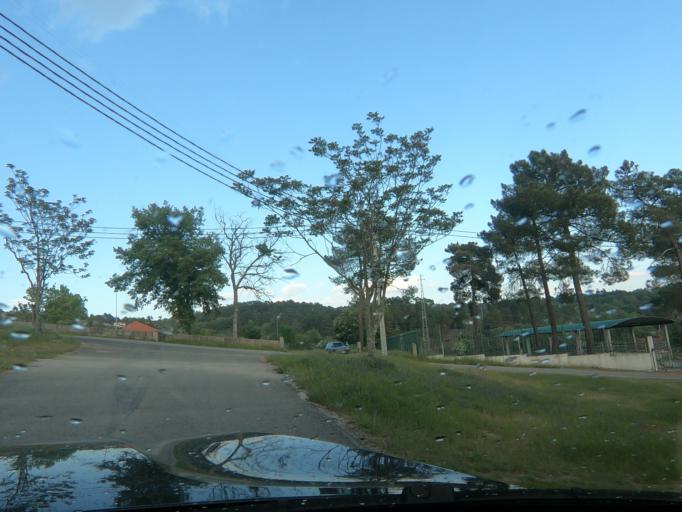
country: PT
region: Vila Real
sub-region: Vila Real
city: Vila Real
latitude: 41.3161
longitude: -7.6747
